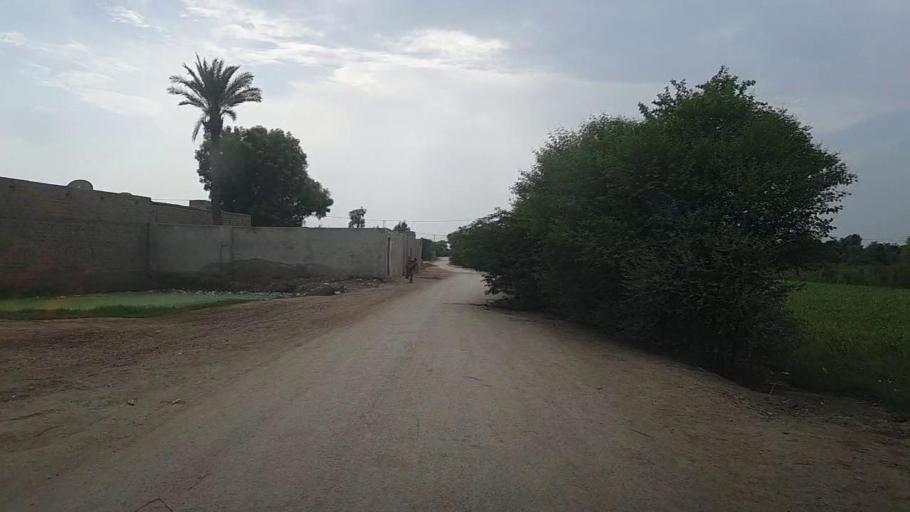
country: PK
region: Sindh
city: Karaundi
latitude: 26.9578
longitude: 68.4218
